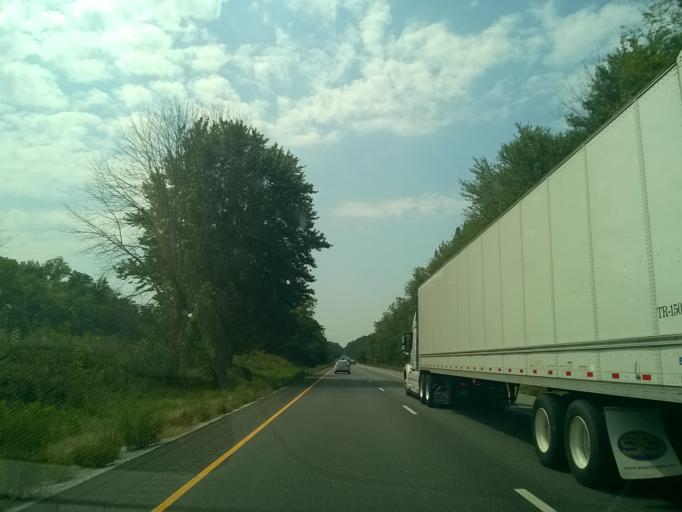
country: US
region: Indiana
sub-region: Clay County
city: Brazil
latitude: 39.4604
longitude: -87.0824
